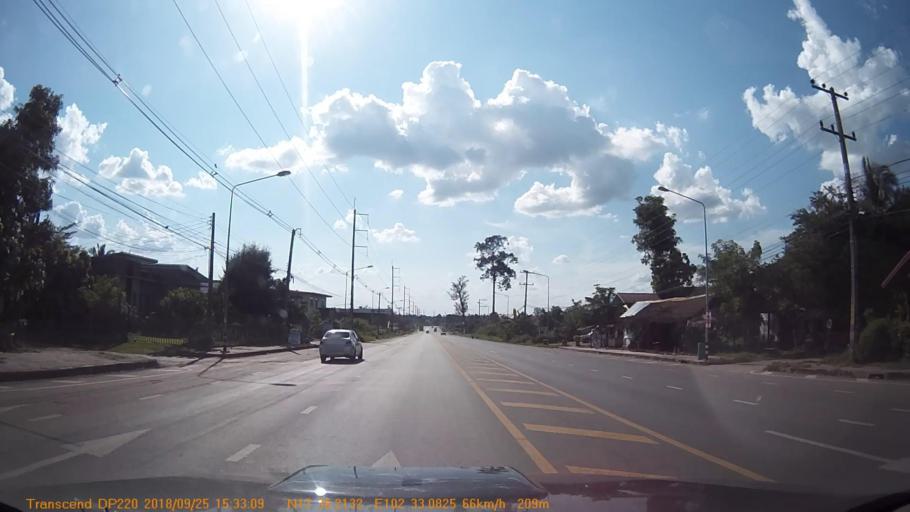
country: TH
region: Changwat Udon Thani
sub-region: Amphoe Ban Phue
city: Ban Phue
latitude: 17.6036
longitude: 102.5508
